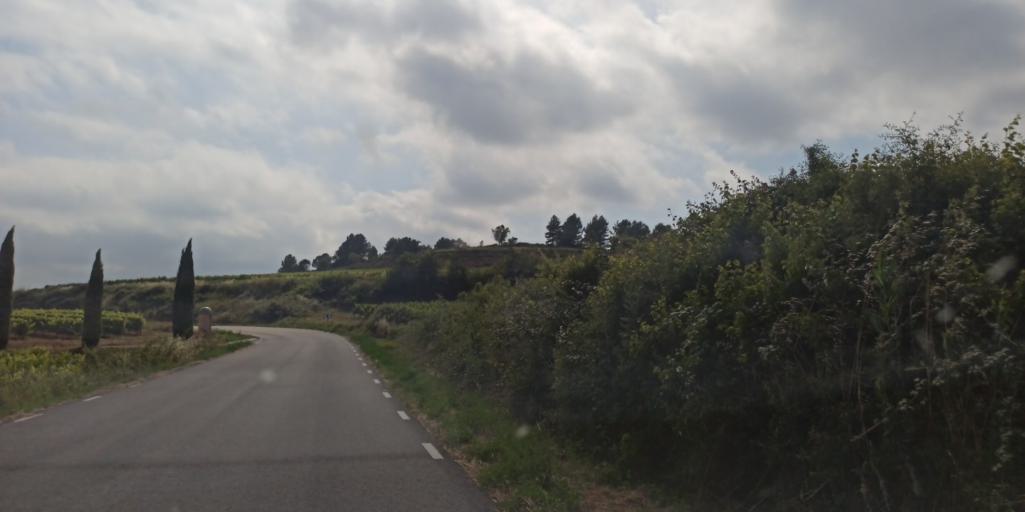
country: ES
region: Catalonia
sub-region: Provincia de Barcelona
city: Sant Joan de Mediona
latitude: 41.4731
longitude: 1.6019
